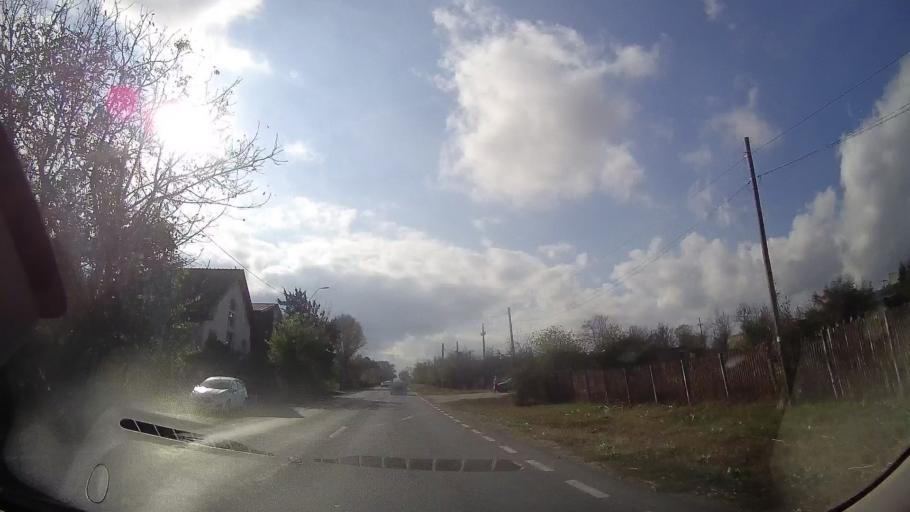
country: RO
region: Constanta
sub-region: Comuna Agigea
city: Agigea
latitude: 44.0876
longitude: 28.6093
